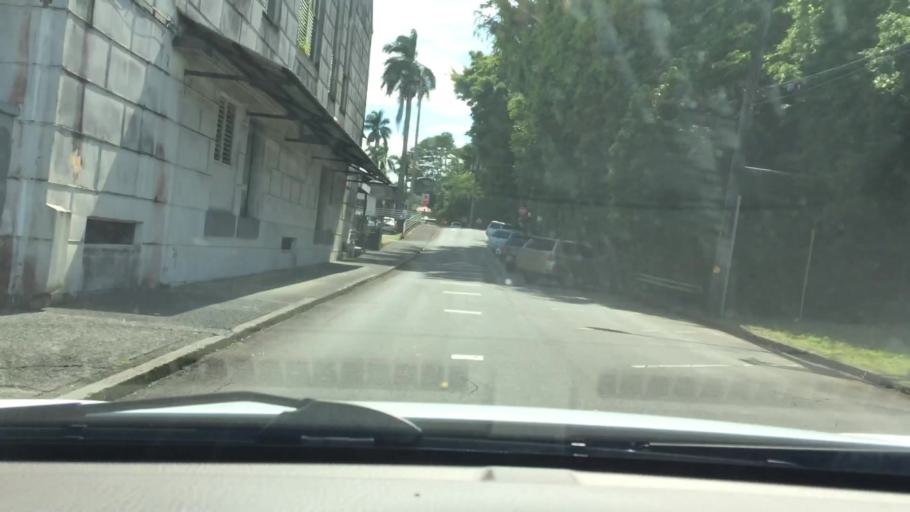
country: US
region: Hawaii
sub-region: Hawaii County
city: Hilo
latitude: 19.7274
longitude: -155.0878
